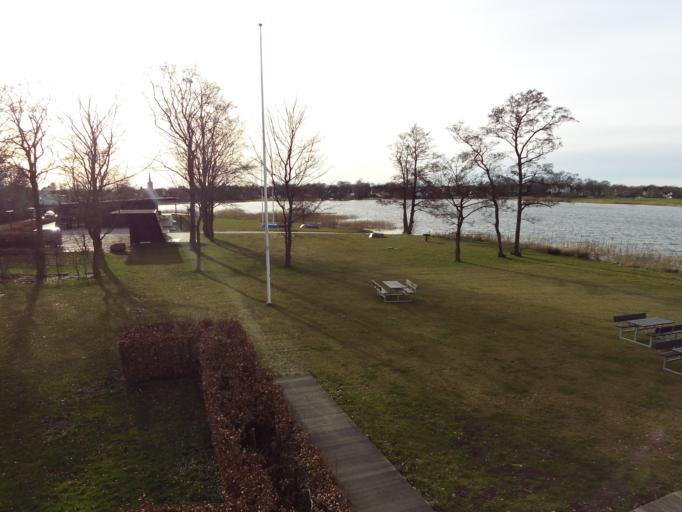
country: DK
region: South Denmark
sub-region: Kolding Kommune
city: Vamdrup
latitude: 55.3584
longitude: 9.2103
